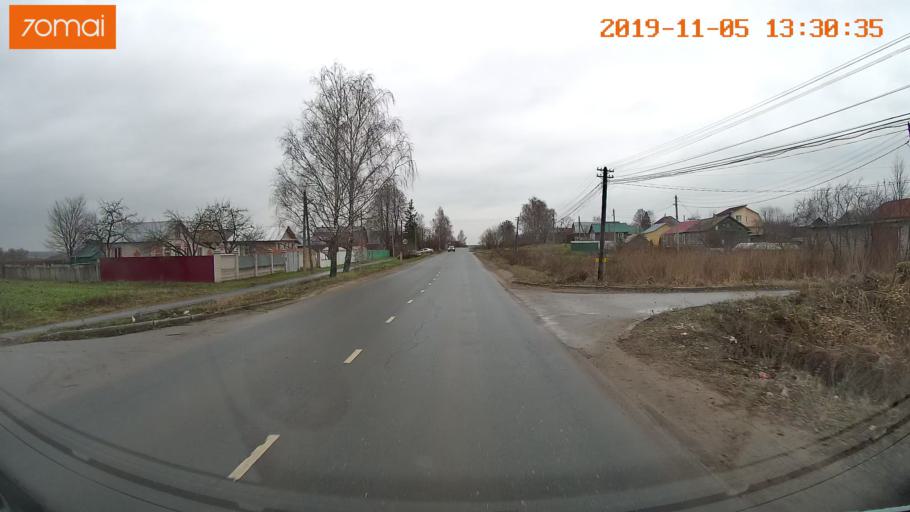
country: RU
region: Ivanovo
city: Shuya
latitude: 56.8681
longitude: 41.3952
